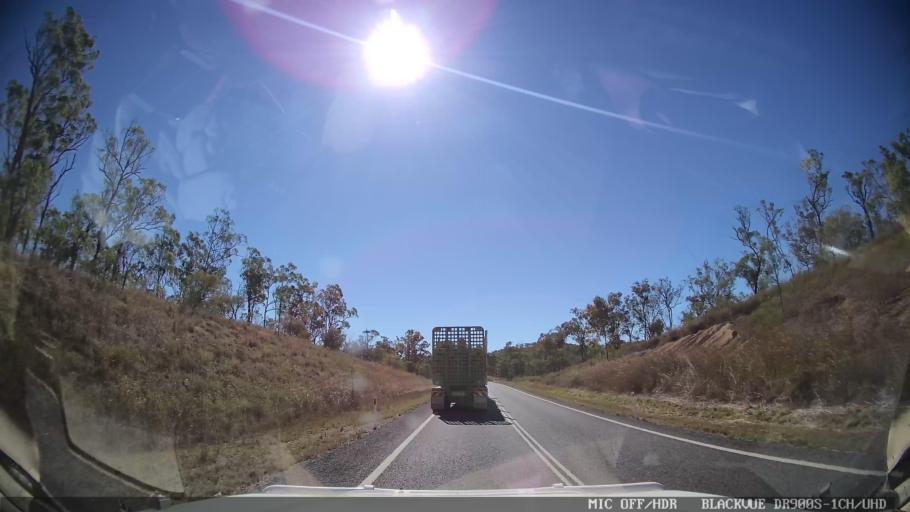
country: AU
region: Queensland
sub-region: Gladstone
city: Toolooa
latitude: -24.1534
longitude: 151.2105
